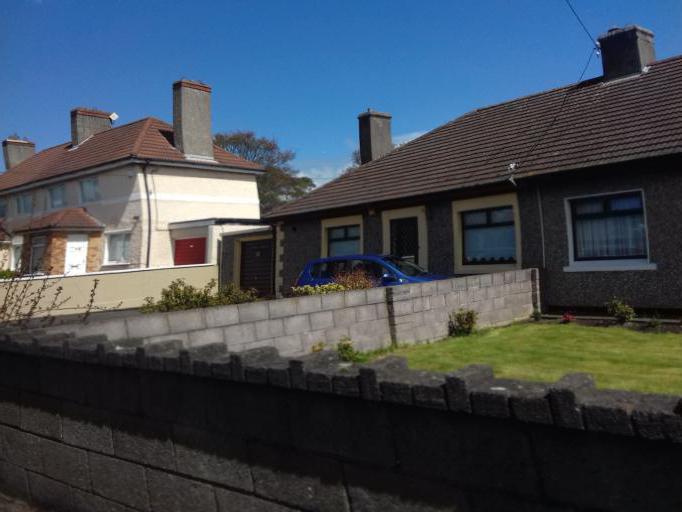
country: IE
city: Killester
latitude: 53.3767
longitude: -6.2041
